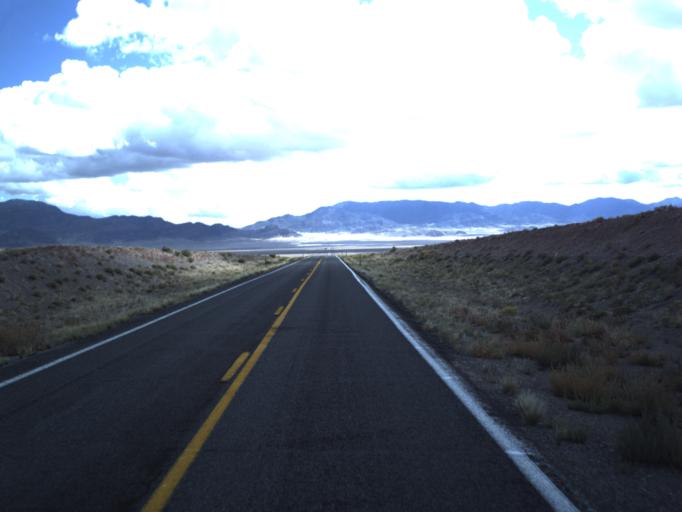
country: US
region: Utah
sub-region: Beaver County
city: Milford
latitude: 38.5671
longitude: -113.7761
